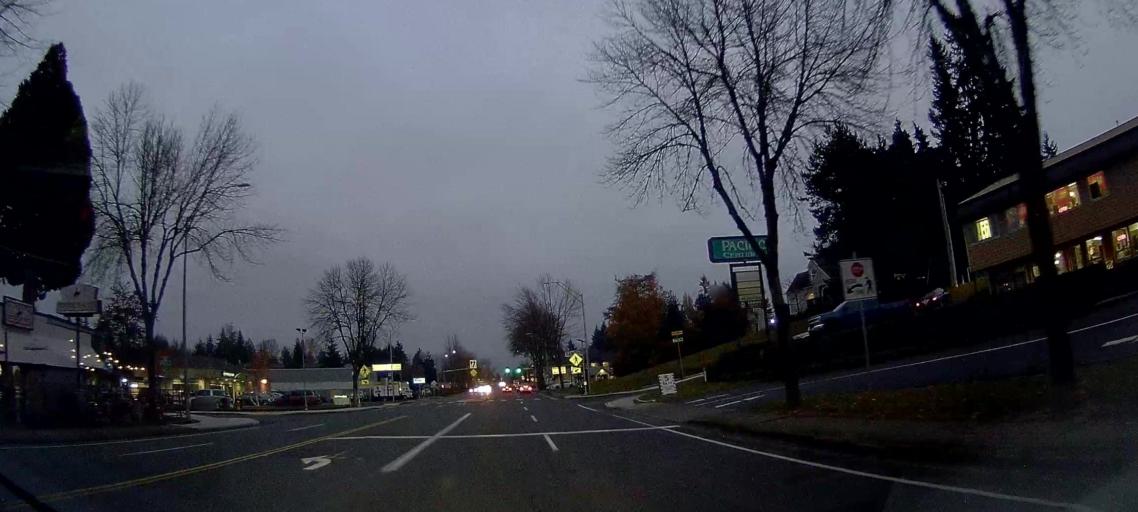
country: US
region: Washington
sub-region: Thurston County
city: Lacey
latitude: 47.0433
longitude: -122.8612
